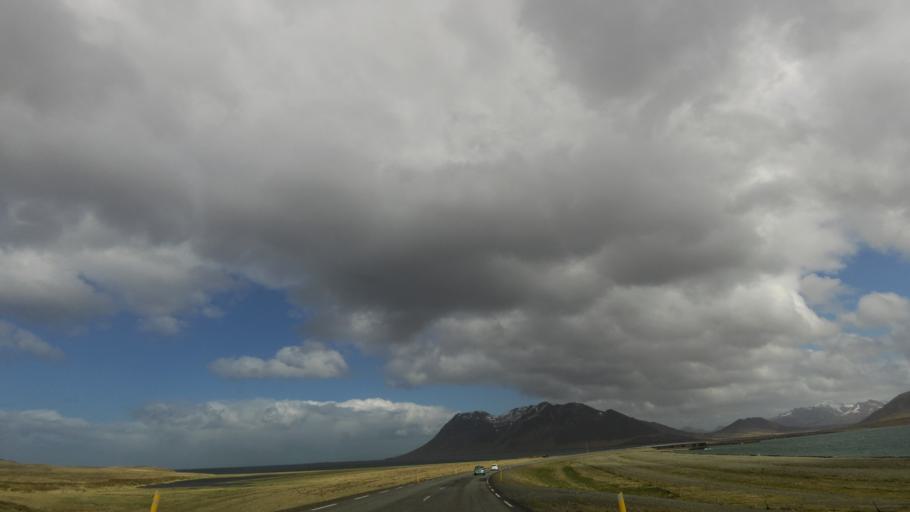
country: IS
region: West
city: Stykkisholmur
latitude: 64.9654
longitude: -23.1331
